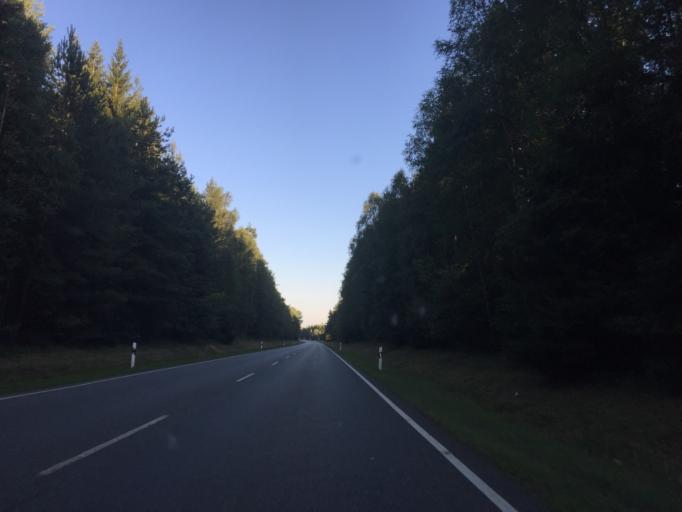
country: DE
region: Bavaria
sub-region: Upper Palatinate
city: Schwarzenbach
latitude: 49.7292
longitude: 11.9617
